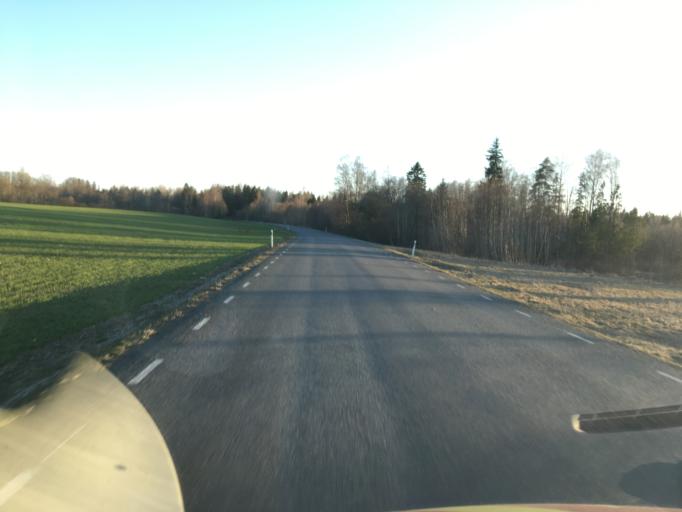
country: EE
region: Raplamaa
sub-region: Kehtna vald
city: Kehtna
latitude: 59.0345
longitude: 24.9248
